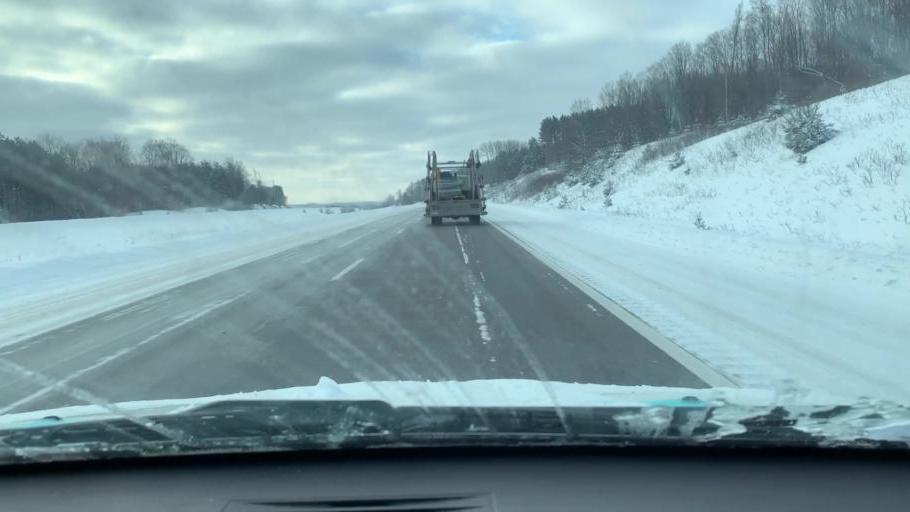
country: US
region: Michigan
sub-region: Wexford County
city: Manton
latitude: 44.4436
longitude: -85.3954
